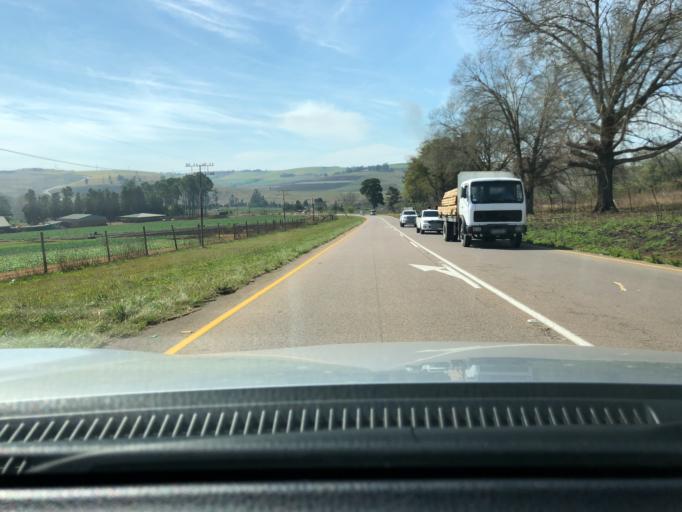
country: ZA
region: KwaZulu-Natal
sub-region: uMgungundlovu District Municipality
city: Richmond
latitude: -29.7779
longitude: 30.3532
